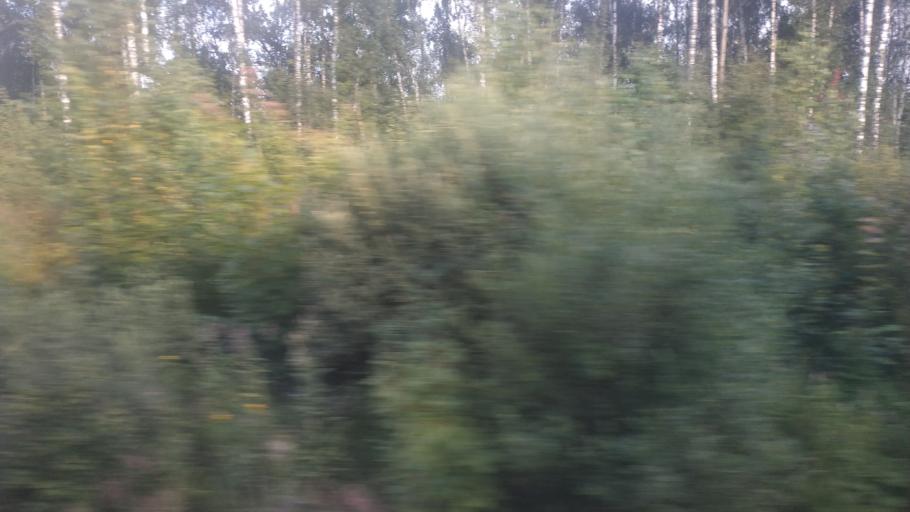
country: RU
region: Moskovskaya
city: Kerva
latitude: 55.5515
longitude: 39.6930
